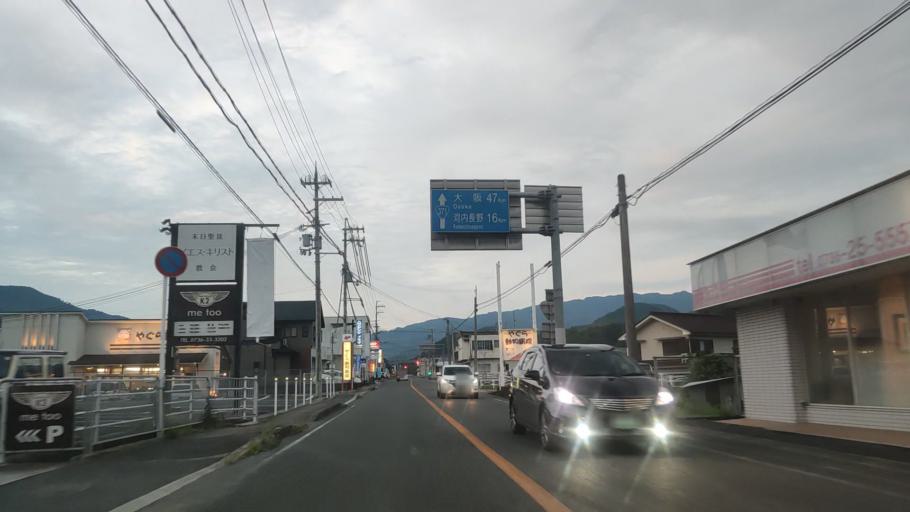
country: JP
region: Wakayama
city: Hashimoto
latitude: 34.3386
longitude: 135.6057
